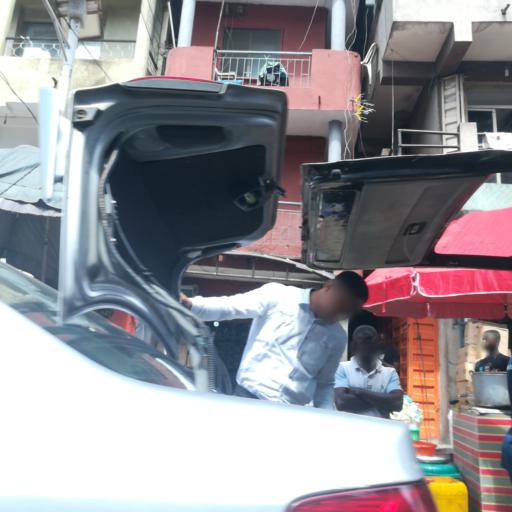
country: NG
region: Lagos
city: Lagos
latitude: 6.4630
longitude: 3.3894
